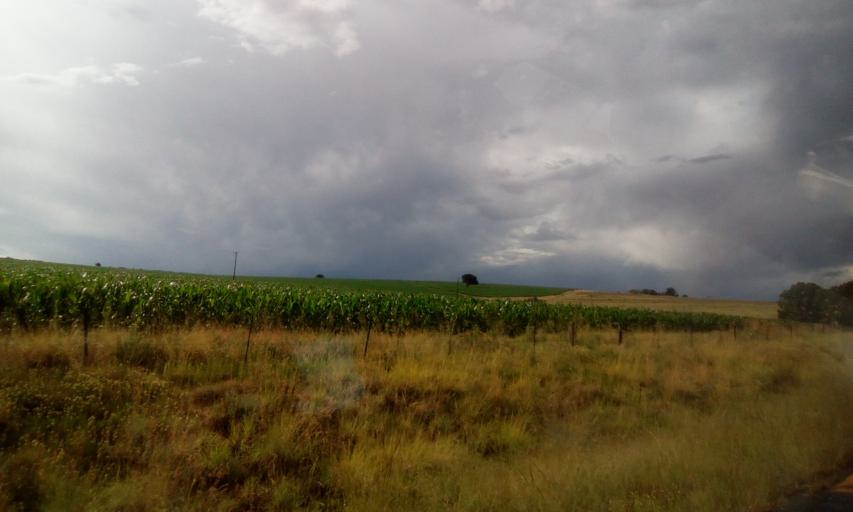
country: ZA
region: Orange Free State
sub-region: Thabo Mofutsanyana District Municipality
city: Ladybrand
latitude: -29.2413
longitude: 27.4490
